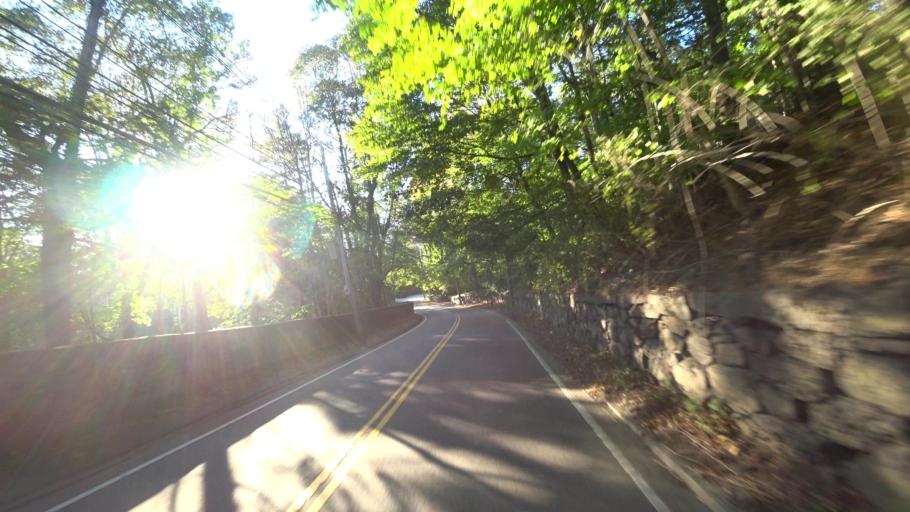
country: US
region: Massachusetts
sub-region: Norfolk County
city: Brookline
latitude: 42.3219
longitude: -71.1342
